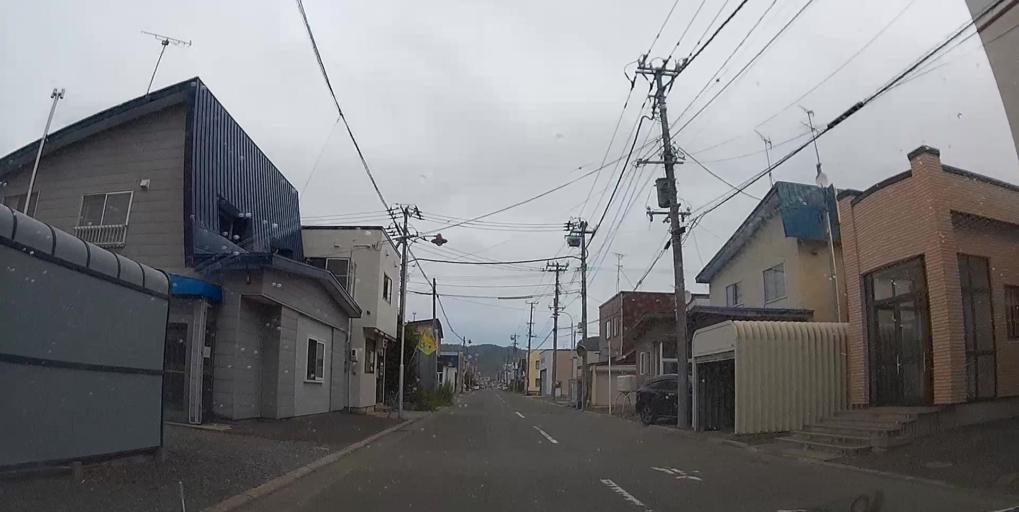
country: JP
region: Hokkaido
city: Iwanai
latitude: 42.4247
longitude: 140.0109
